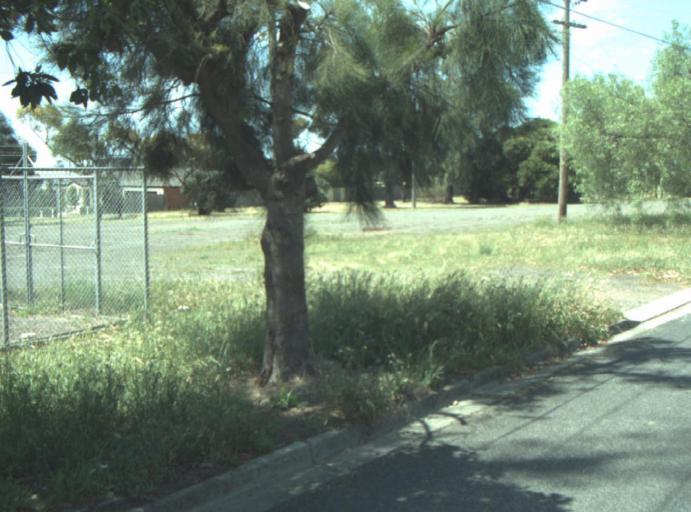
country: AU
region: Victoria
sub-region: Greater Geelong
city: Hamlyn Heights
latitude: -38.1367
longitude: 144.3187
